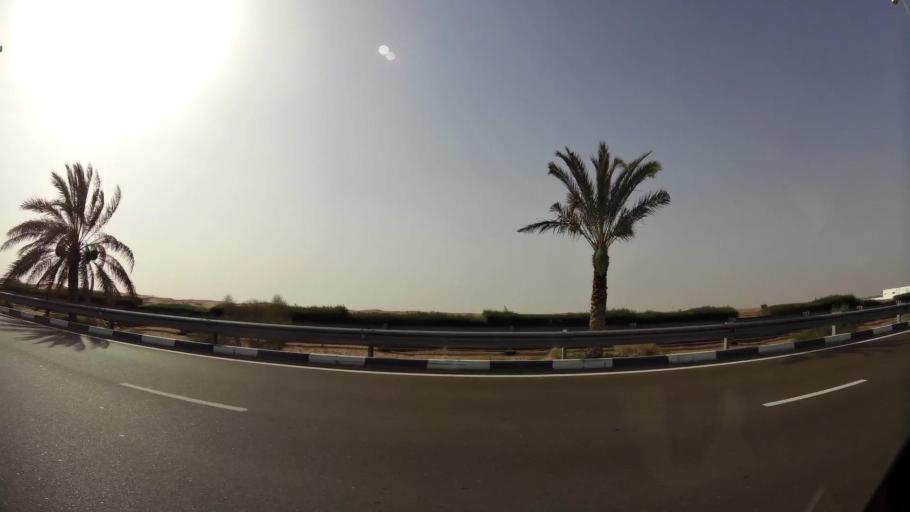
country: AE
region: Abu Dhabi
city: Al Ain
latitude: 24.2175
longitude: 55.6369
